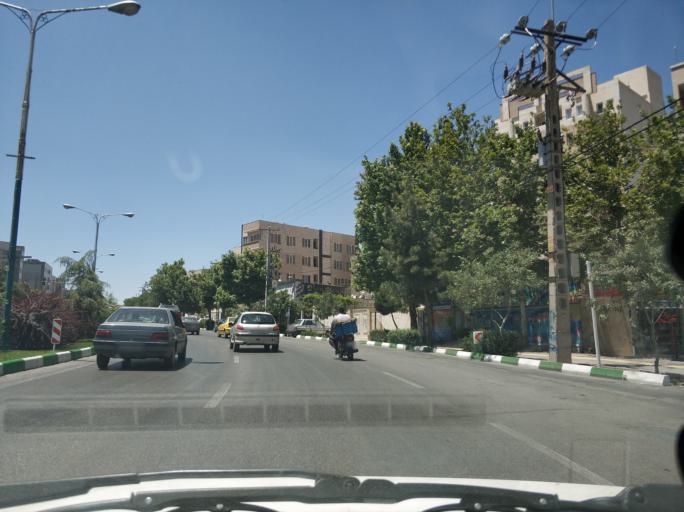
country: IR
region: Razavi Khorasan
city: Mashhad
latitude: 36.3118
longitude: 59.4960
